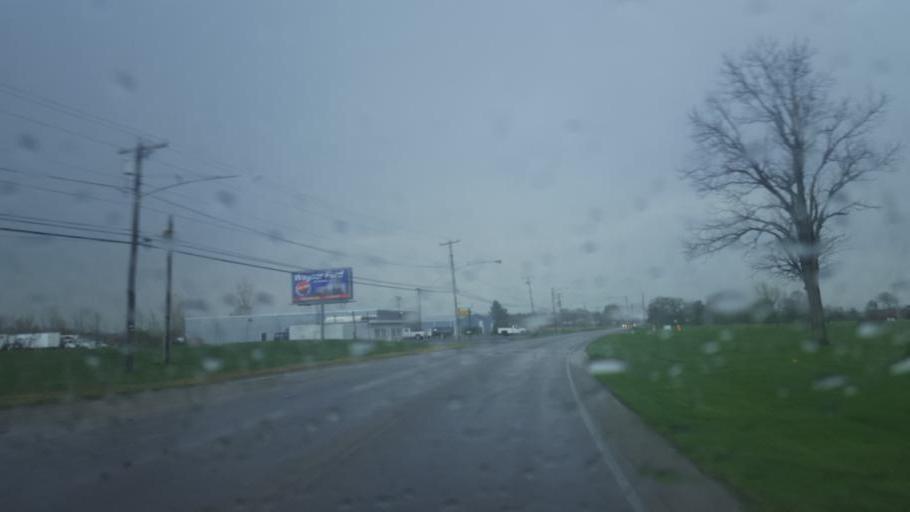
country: US
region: Ohio
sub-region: Seneca County
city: Fostoria
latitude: 41.1463
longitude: -83.4019
